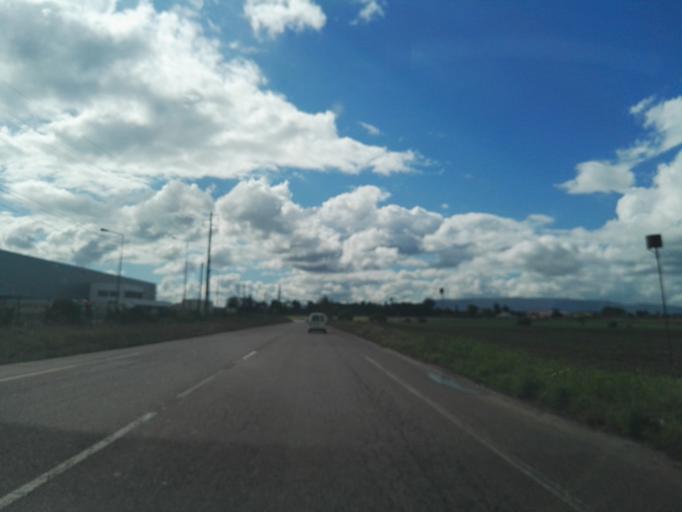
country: PT
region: Santarem
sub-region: Torres Novas
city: Riachos
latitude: 39.4450
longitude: -8.4972
